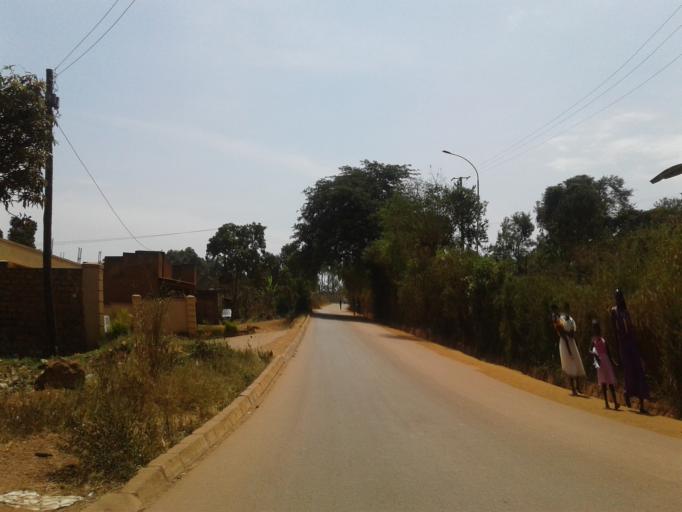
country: UG
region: Central Region
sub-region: Kampala District
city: Kampala
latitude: 0.2658
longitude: 32.6275
